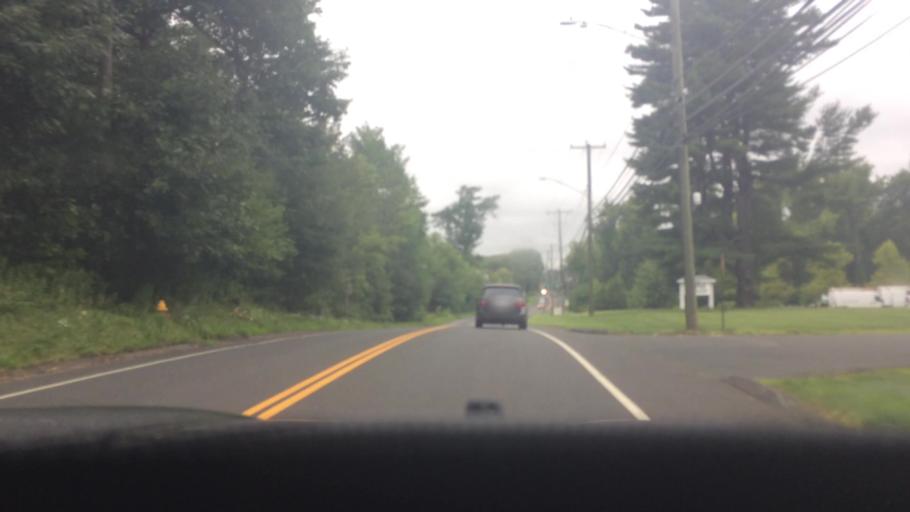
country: US
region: Connecticut
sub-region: Hartford County
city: Blue Hills
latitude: 41.7988
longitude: -72.7229
